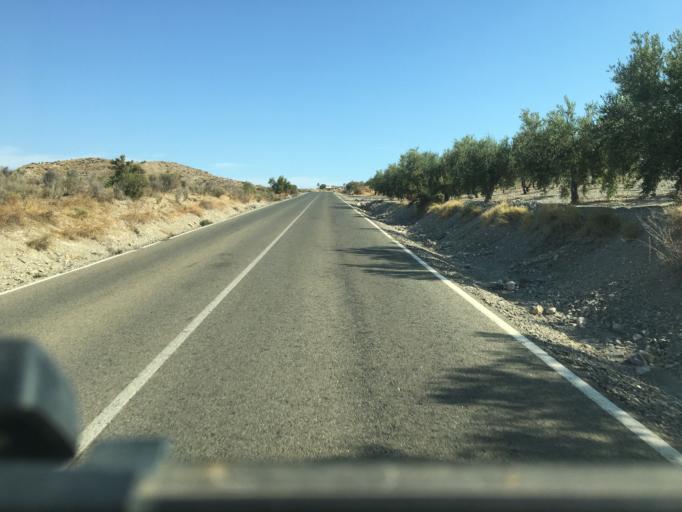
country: ES
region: Andalusia
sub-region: Provincia de Almeria
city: Huercal-Overa
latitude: 37.4254
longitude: -1.9709
